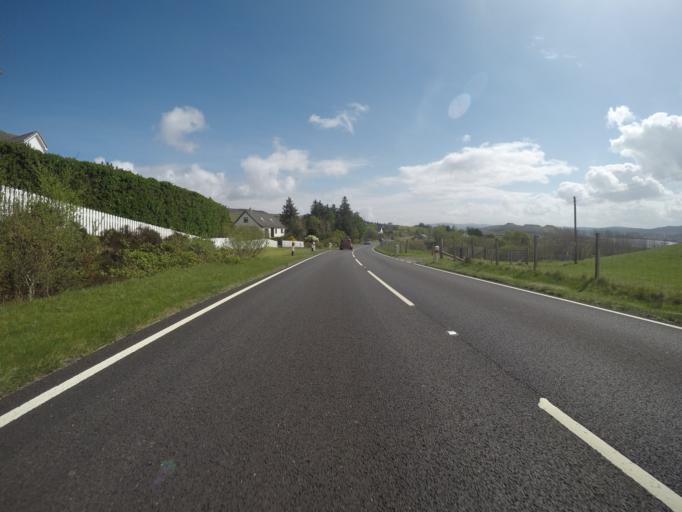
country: GB
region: Scotland
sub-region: Highland
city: Portree
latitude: 57.4993
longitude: -6.3248
